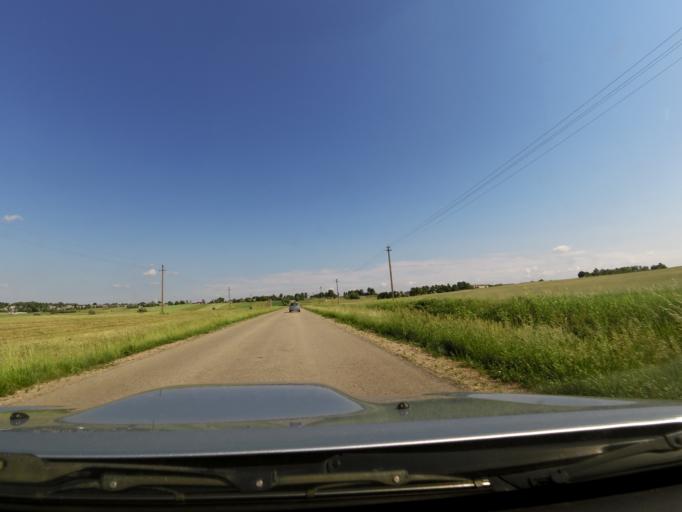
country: LT
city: Vilkaviskis
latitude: 54.5048
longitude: 23.0088
